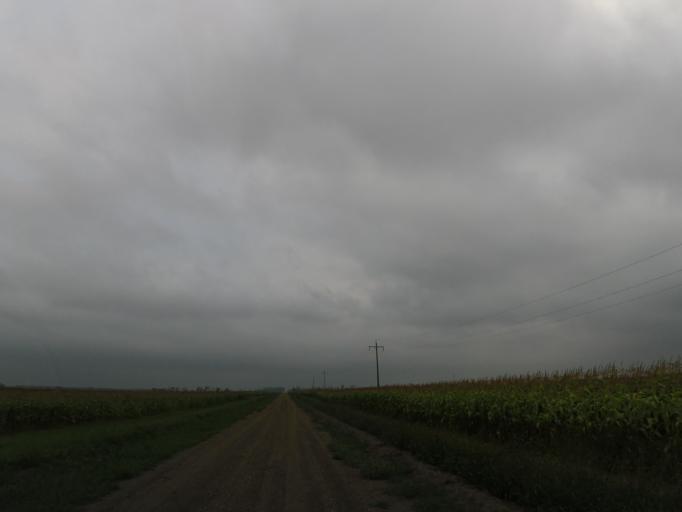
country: US
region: North Dakota
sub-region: Walsh County
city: Grafton
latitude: 48.5320
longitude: -97.1687
